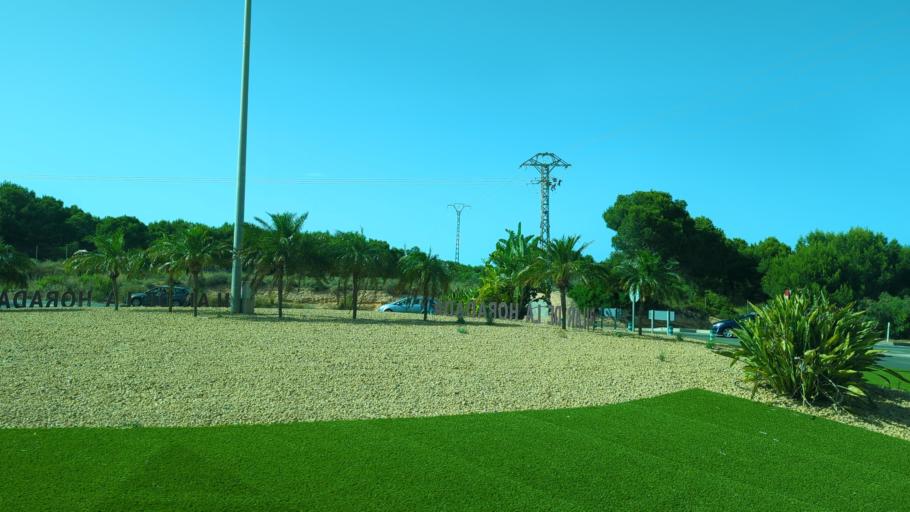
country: ES
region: Valencia
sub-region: Provincia de Alicante
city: Pilar de la Horadada
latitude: 37.8913
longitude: -0.7632
